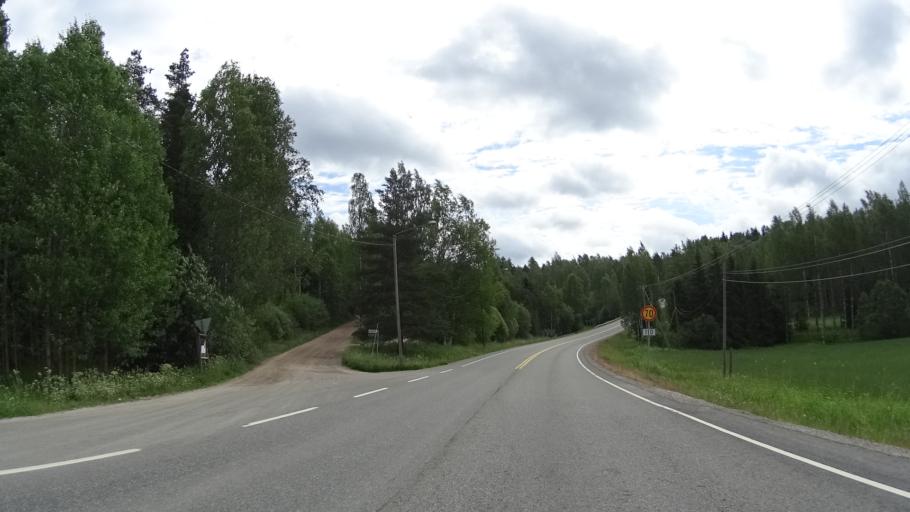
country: FI
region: Uusimaa
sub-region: Helsinki
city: Vihti
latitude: 60.2933
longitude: 24.3985
